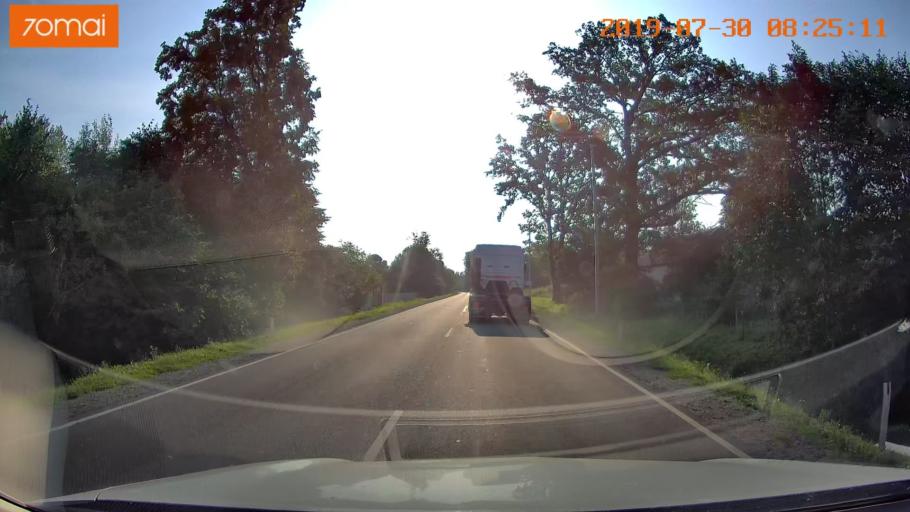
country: RU
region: Kaliningrad
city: Chernyakhovsk
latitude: 54.6238
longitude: 21.5750
